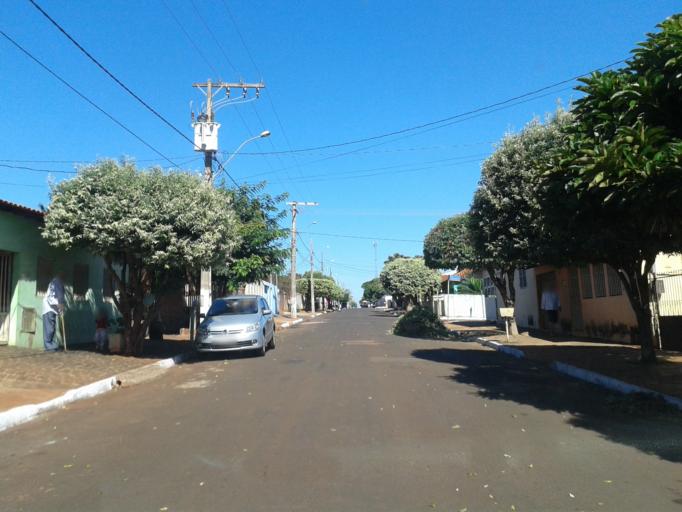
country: BR
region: Minas Gerais
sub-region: Santa Vitoria
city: Santa Vitoria
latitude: -18.8372
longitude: -50.1201
